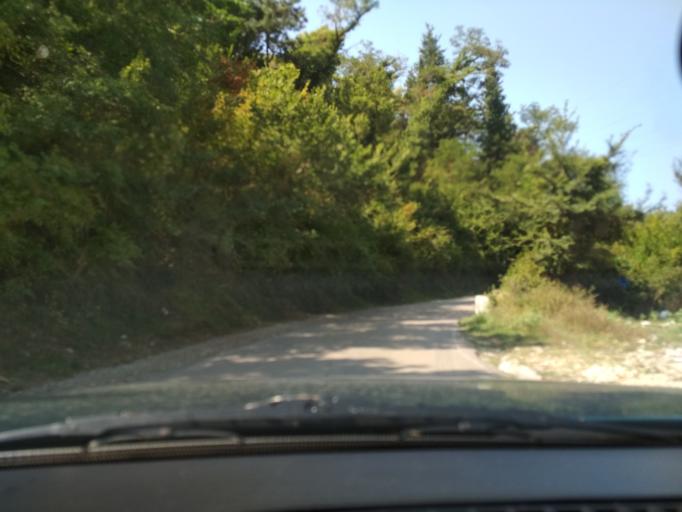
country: ME
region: Kotor
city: Kotor
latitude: 42.4010
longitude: 18.7622
